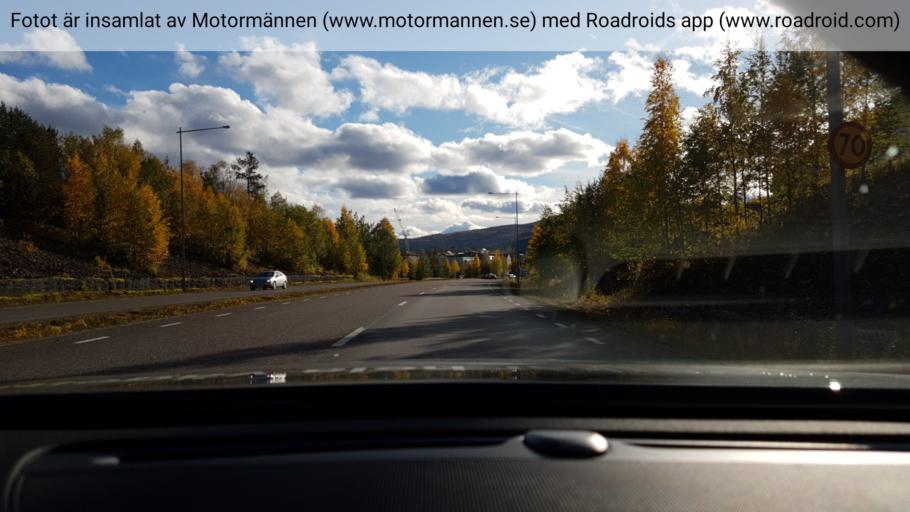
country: SE
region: Norrbotten
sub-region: Gallivare Kommun
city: Gaellivare
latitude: 67.1409
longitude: 20.6622
